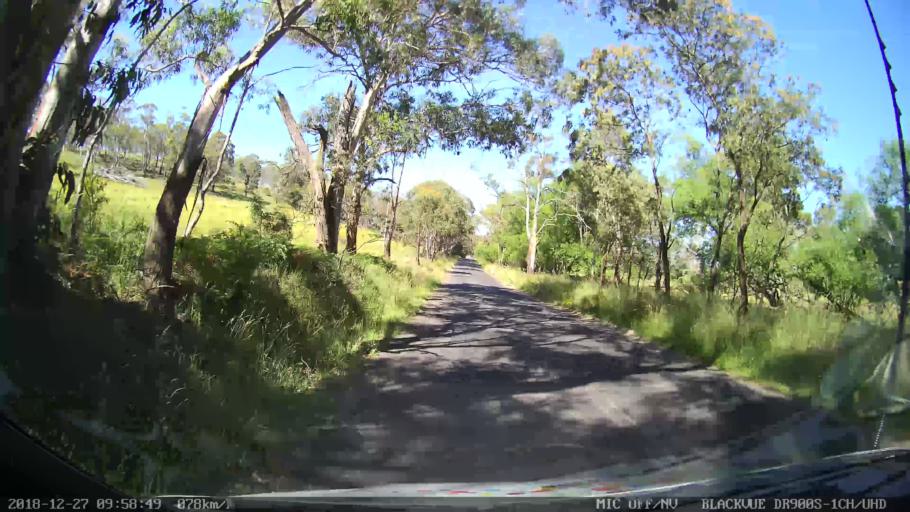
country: AU
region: New South Wales
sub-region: Lithgow
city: Portland
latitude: -33.4307
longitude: 149.9593
